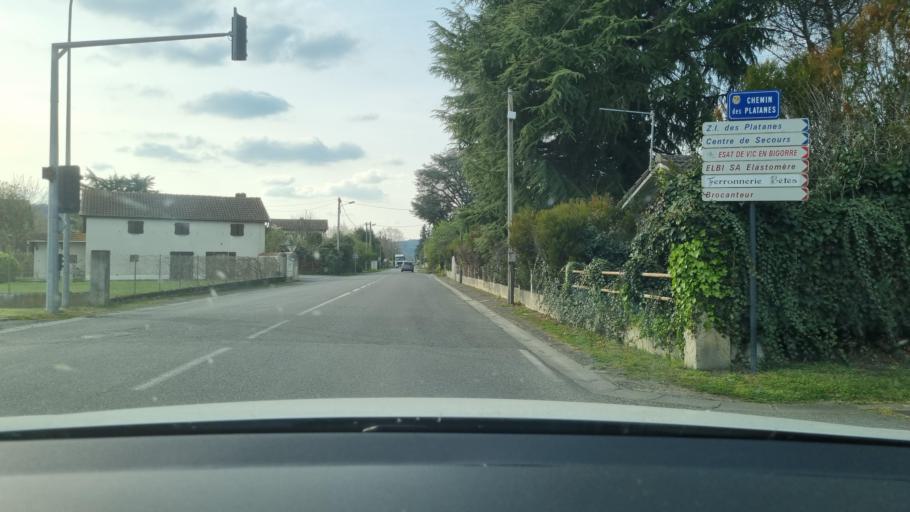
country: FR
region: Midi-Pyrenees
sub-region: Departement des Hautes-Pyrenees
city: Vic-en-Bigorre
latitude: 43.3861
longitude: 0.0446
